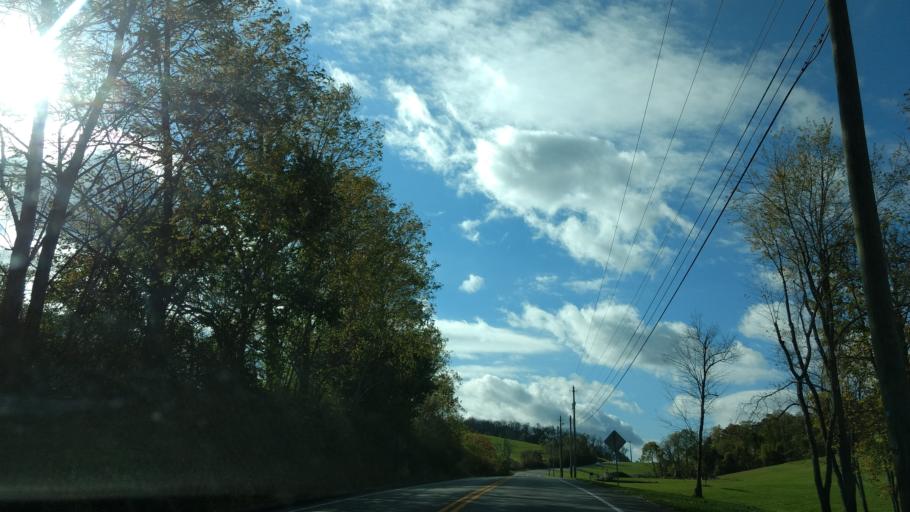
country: US
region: Pennsylvania
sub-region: Westmoreland County
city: Fellsburg
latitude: 40.1671
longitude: -79.8183
